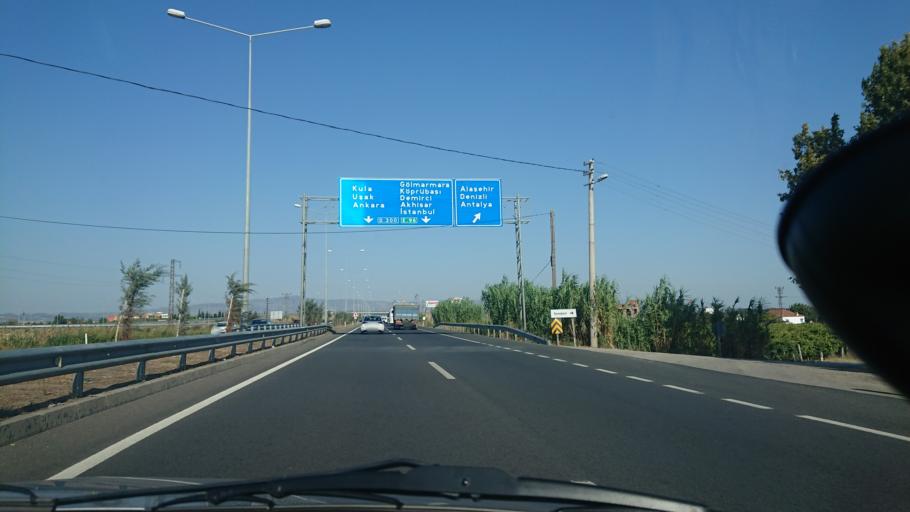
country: TR
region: Manisa
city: Salihli
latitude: 38.4983
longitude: 28.1962
